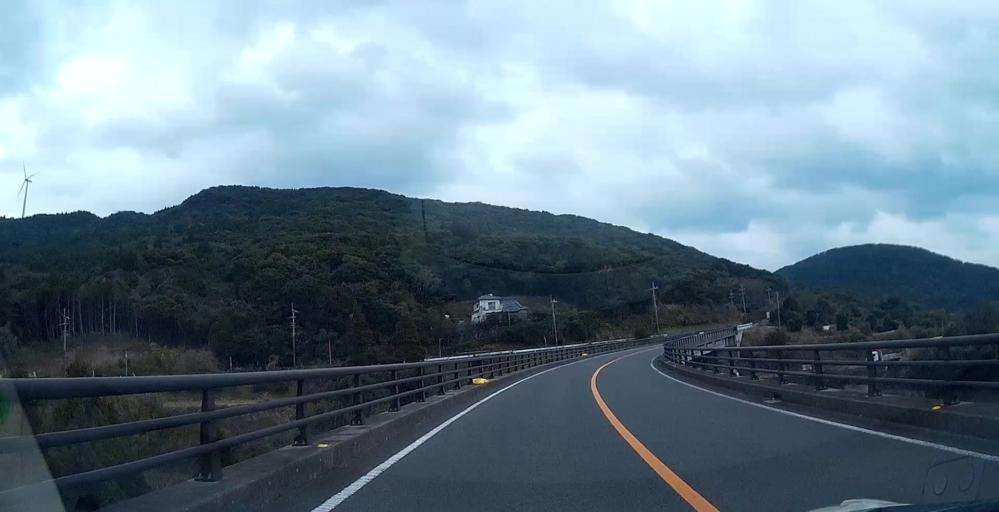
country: JP
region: Kagoshima
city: Akune
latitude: 32.1047
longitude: 130.1504
